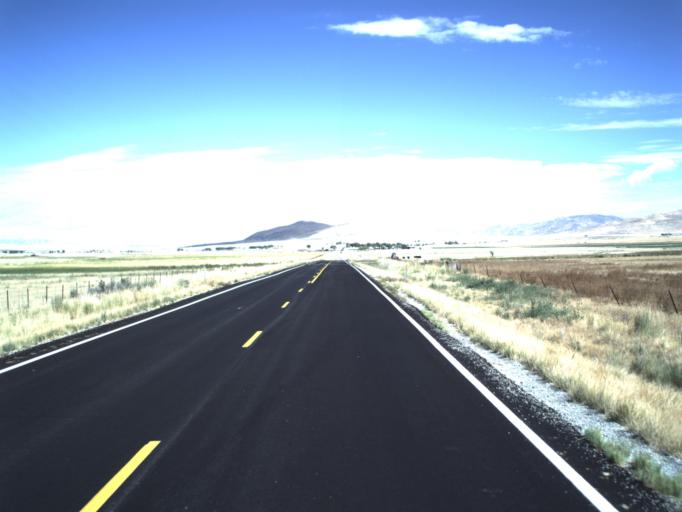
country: US
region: Utah
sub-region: Box Elder County
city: Tremonton
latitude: 41.7498
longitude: -112.4345
